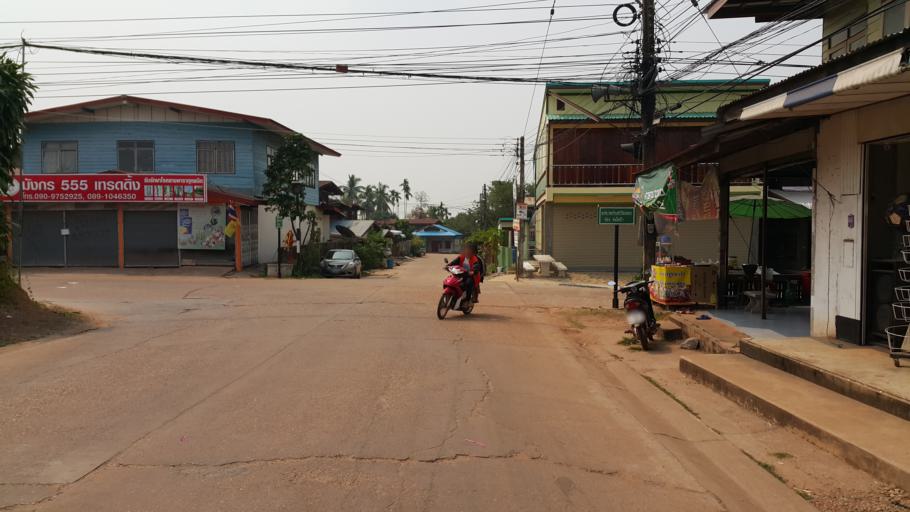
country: TH
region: Changwat Bueng Kan
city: Bueng Khong Long
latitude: 17.9593
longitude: 104.0445
